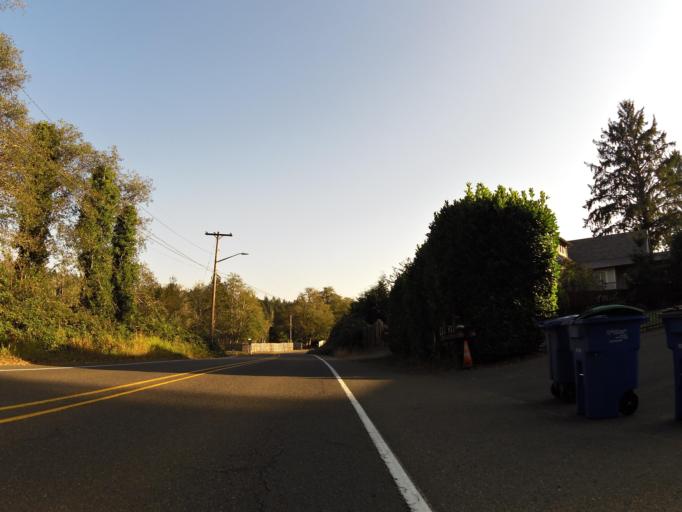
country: US
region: Oregon
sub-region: Lincoln County
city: Lincoln City
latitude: 45.0024
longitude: -123.9792
